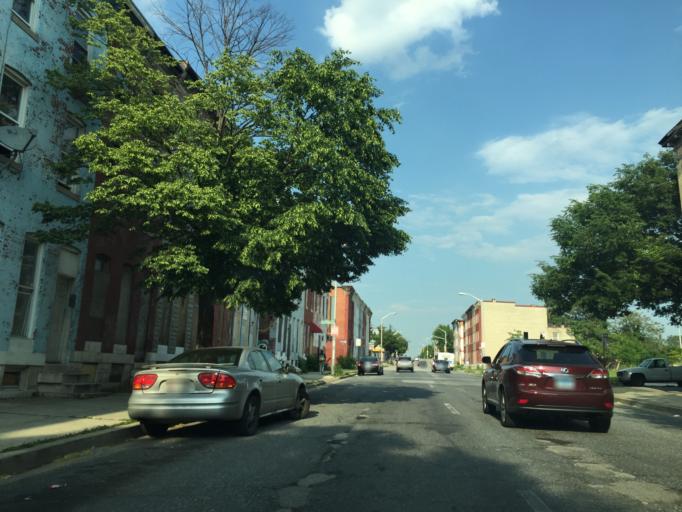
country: US
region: Maryland
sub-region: City of Baltimore
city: Baltimore
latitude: 39.3037
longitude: -76.6101
